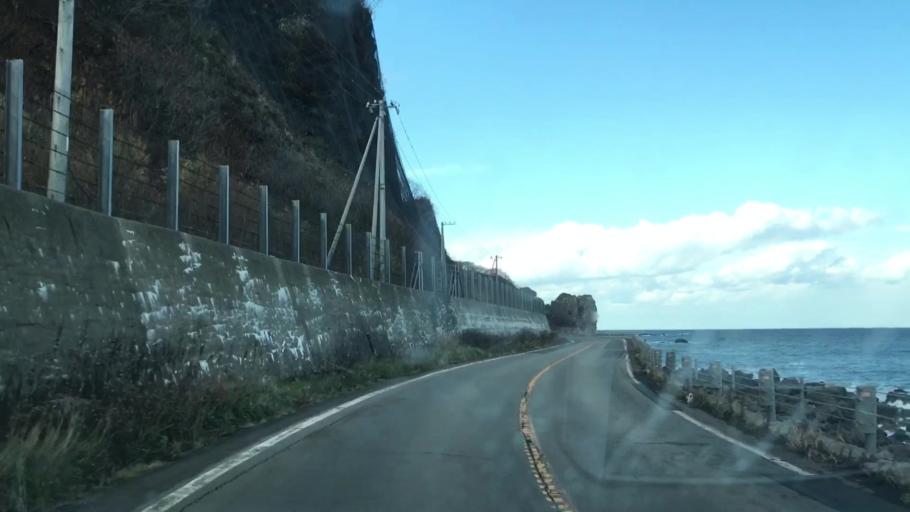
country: JP
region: Hokkaido
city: Iwanai
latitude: 43.3292
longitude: 140.4212
